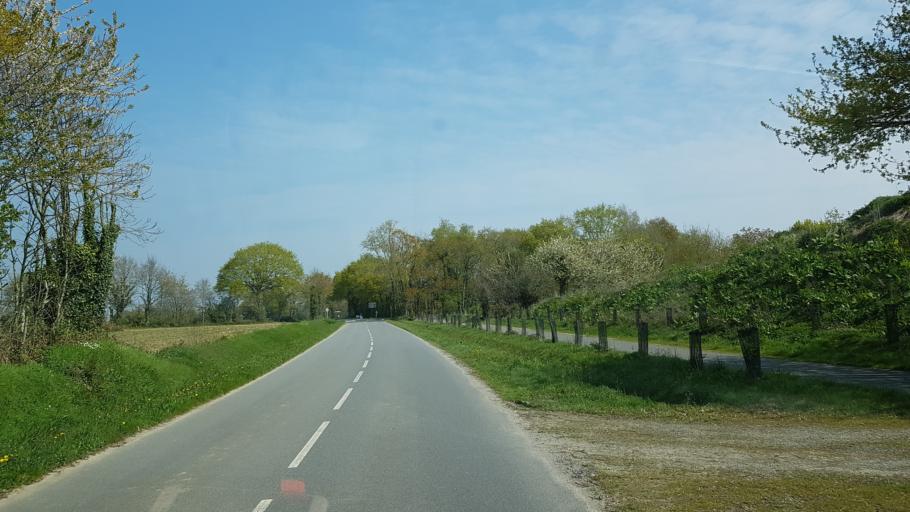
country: FR
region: Brittany
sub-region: Departement du Morbihan
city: Peaule
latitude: 47.5896
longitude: -2.4035
